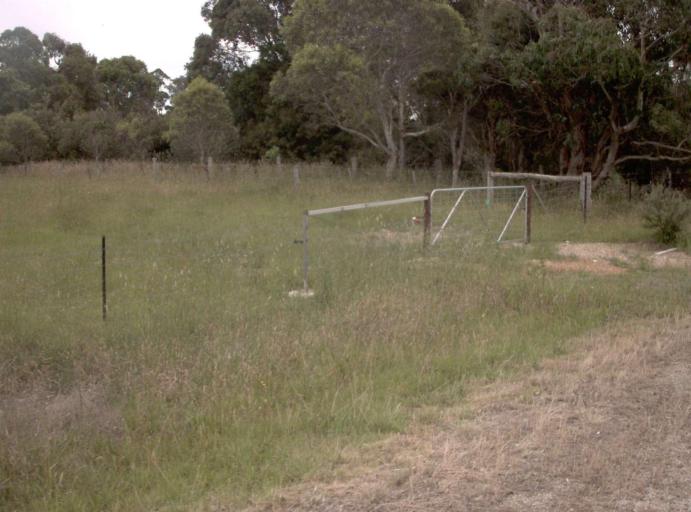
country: AU
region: Victoria
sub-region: East Gippsland
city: Bairnsdale
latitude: -37.8561
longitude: 147.5644
